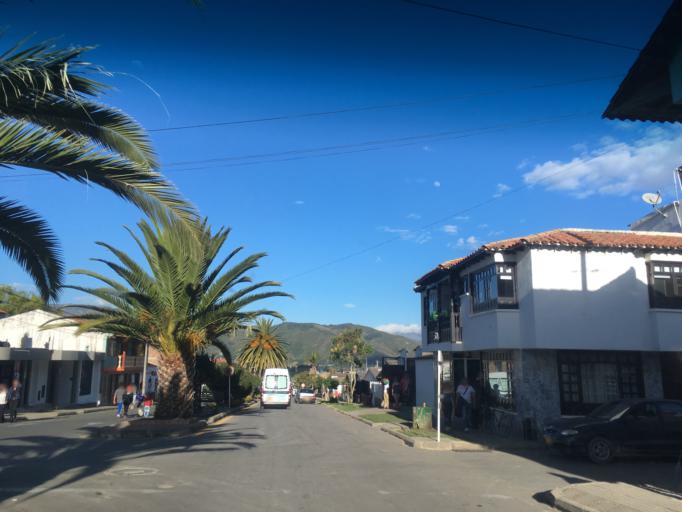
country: CO
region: Boyaca
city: Tibasosa
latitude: 5.7466
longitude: -73.0006
